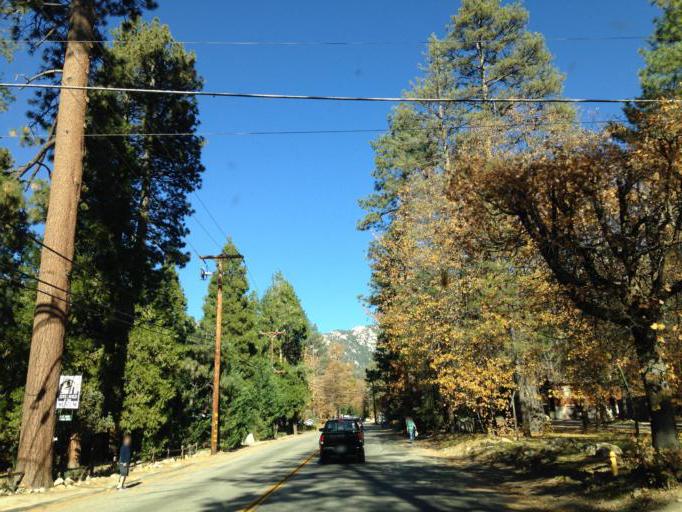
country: US
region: California
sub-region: Riverside County
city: Idyllwild
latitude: 33.7471
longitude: -116.7109
